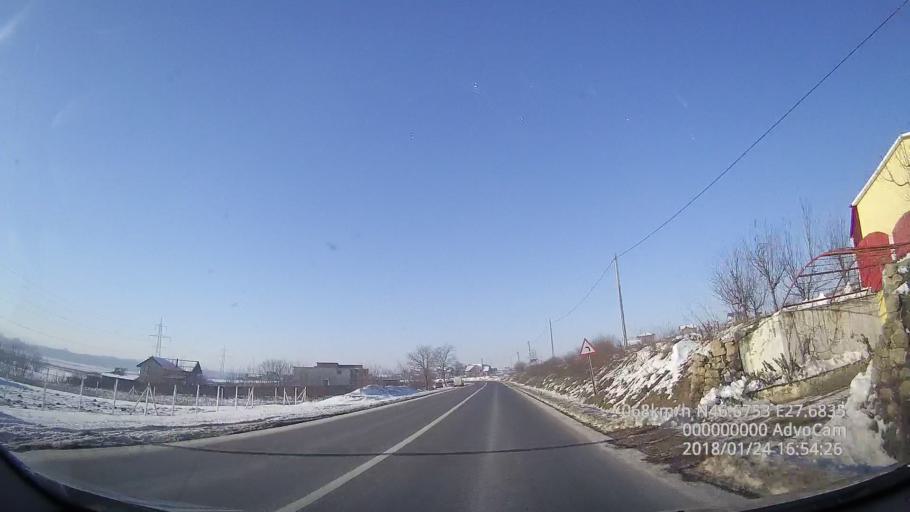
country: RO
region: Vaslui
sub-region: Municipiul Vaslui
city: Brodoc
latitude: 46.6757
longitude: 27.6831
